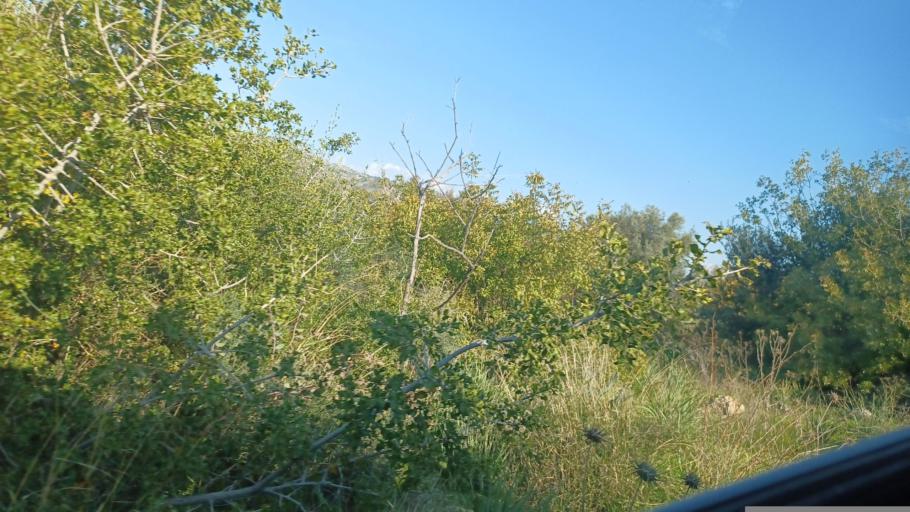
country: CY
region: Pafos
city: Mesogi
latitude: 34.7644
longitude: 32.5609
